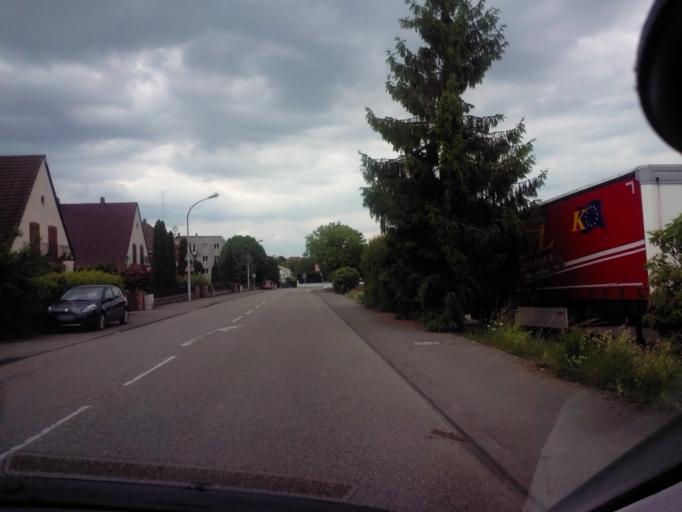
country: FR
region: Alsace
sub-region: Departement du Bas-Rhin
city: Sarre-Union
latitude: 48.9333
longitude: 7.0893
